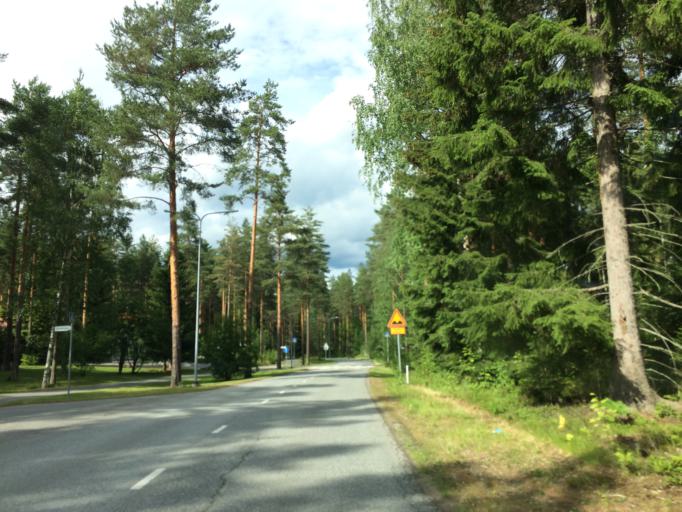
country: FI
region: Haeme
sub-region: Haemeenlinna
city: Turenki
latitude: 60.9338
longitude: 24.6504
